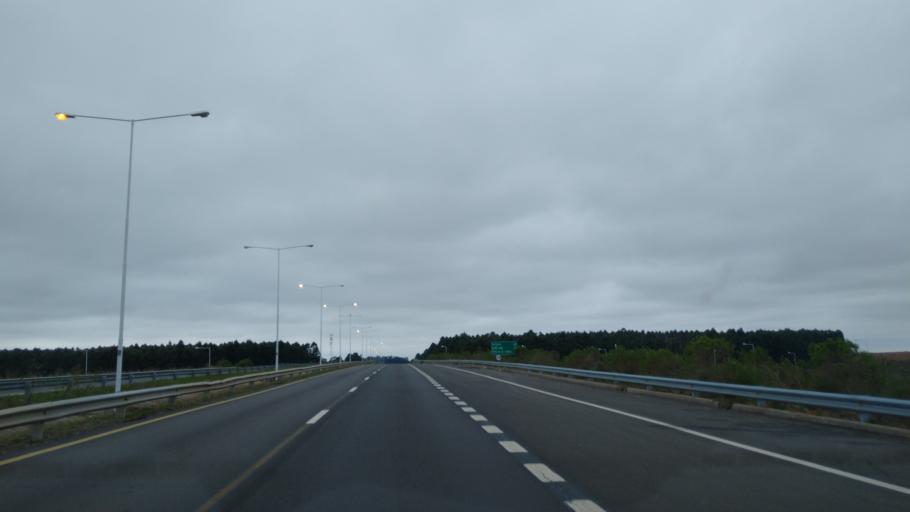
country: AR
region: Corrientes
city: Libertad
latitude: -30.0584
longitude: -57.8149
